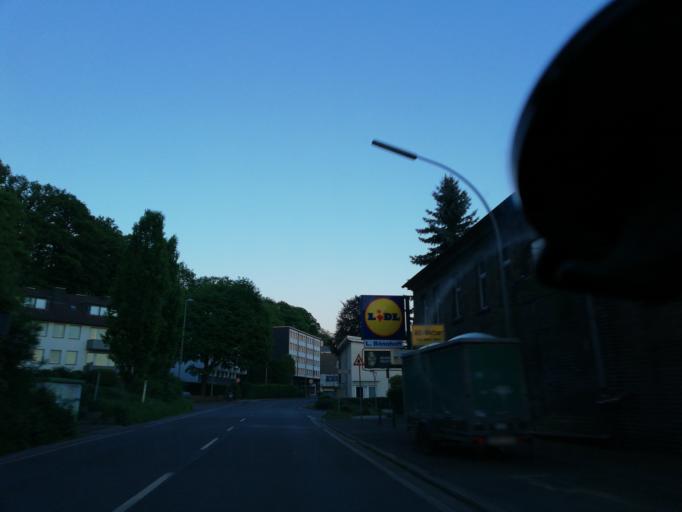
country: DE
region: North Rhine-Westphalia
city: Wetter (Ruhr)
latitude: 51.3897
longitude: 7.3842
